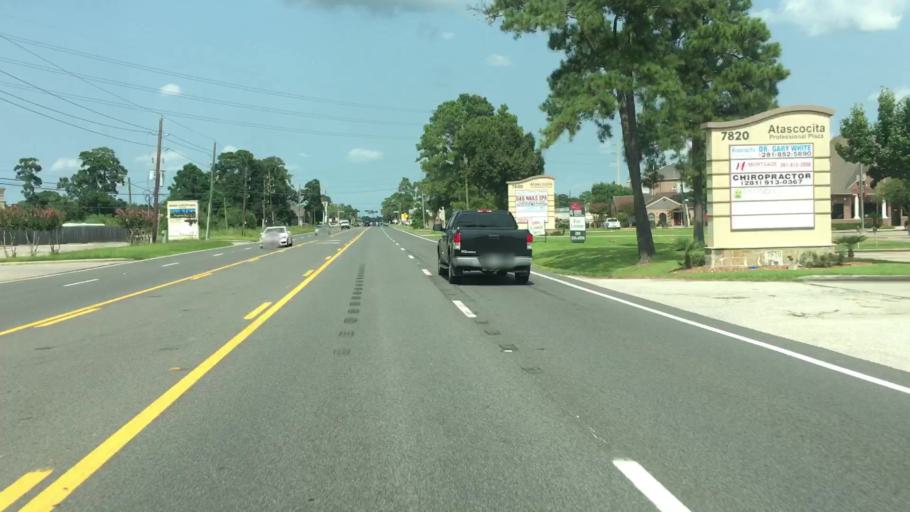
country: US
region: Texas
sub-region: Harris County
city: Atascocita
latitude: 30.0015
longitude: -95.1572
